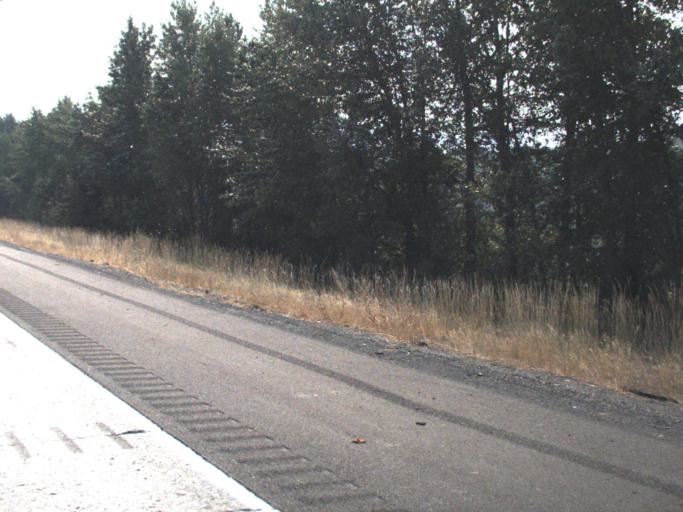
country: US
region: Washington
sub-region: Kittitas County
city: Cle Elum
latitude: 47.1870
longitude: -120.9170
